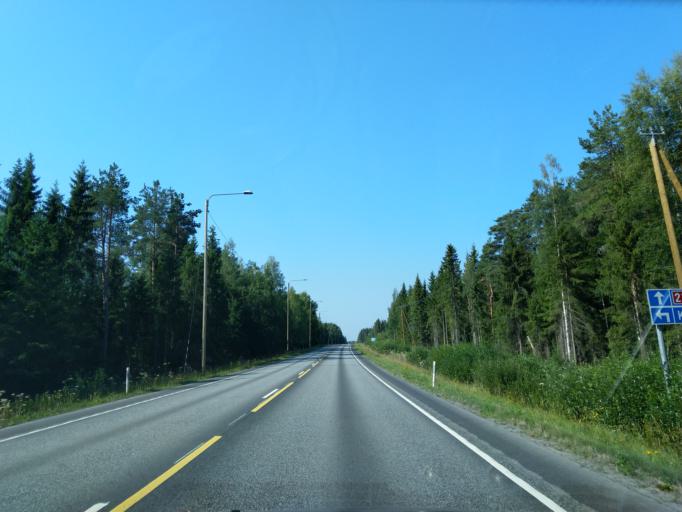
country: FI
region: Satakunta
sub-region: Pori
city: Pomarkku
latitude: 61.7089
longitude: 22.0311
